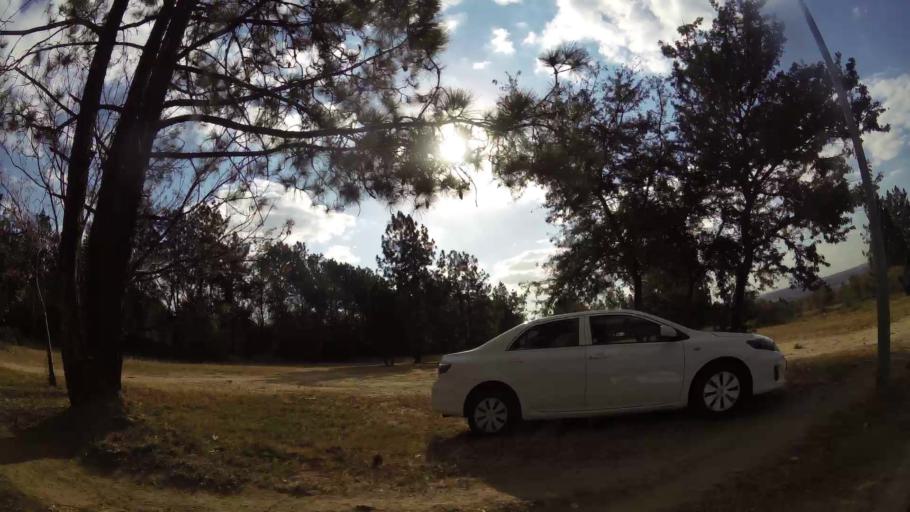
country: ZA
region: Gauteng
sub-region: City of Johannesburg Metropolitan Municipality
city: Diepsloot
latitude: -26.0045
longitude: 28.0210
